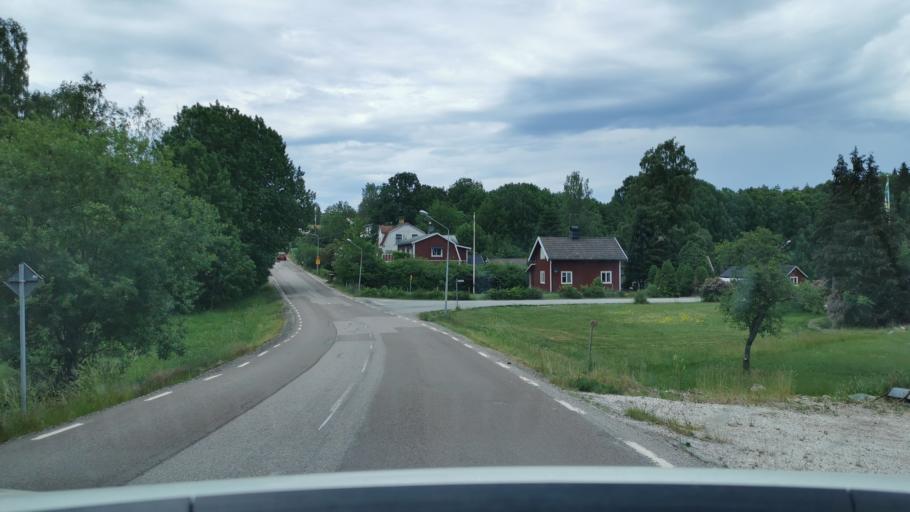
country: SE
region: Vaestra Goetaland
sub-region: Melleruds Kommun
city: Mellerud
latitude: 58.8256
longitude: 12.4139
